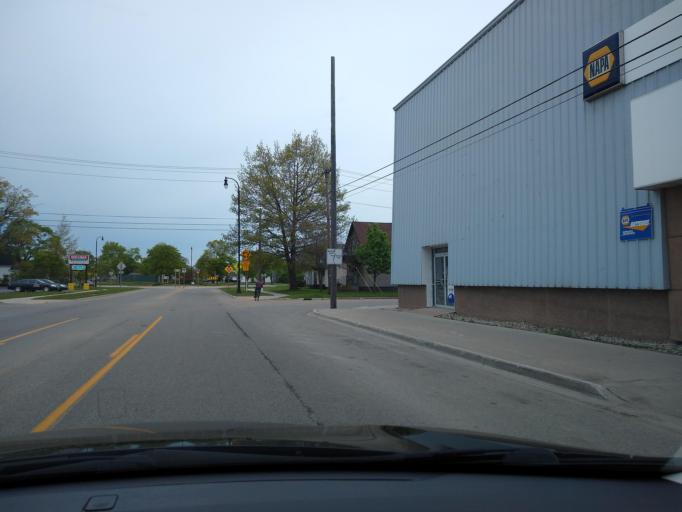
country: US
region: Michigan
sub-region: Delta County
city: Escanaba
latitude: 45.7546
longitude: -87.0717
